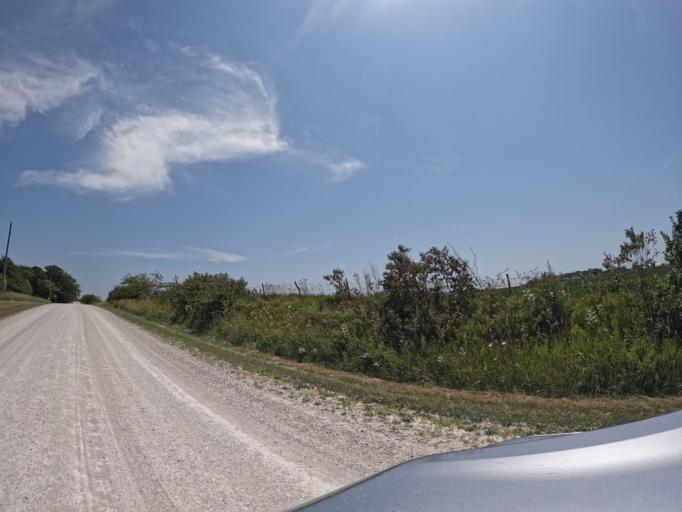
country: US
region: Iowa
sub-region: Henry County
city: Mount Pleasant
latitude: 40.9306
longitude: -91.6203
